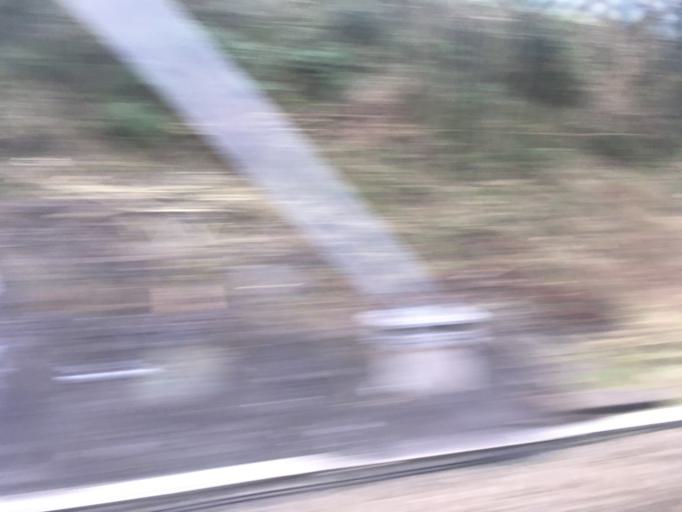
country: GB
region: England
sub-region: South Gloucestershire
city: Chipping Sodbury
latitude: 51.5321
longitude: -2.3959
